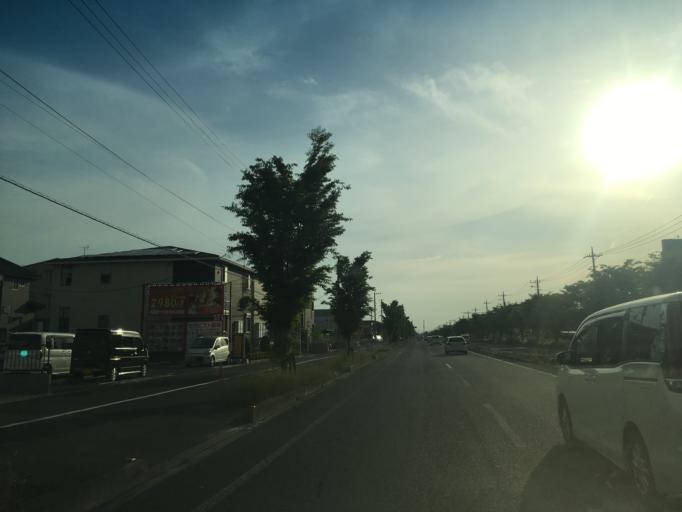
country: JP
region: Saitama
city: Yoshikawa
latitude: 35.8848
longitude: 139.8213
